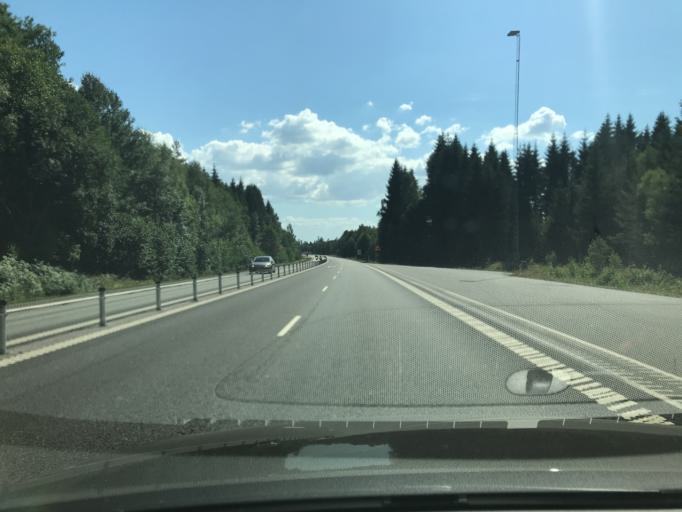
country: SE
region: Skane
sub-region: Osby Kommun
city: Osby
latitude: 56.4074
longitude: 14.0429
